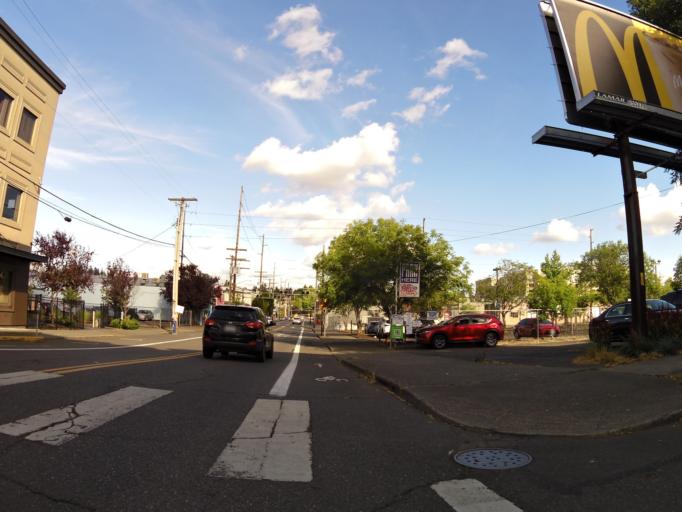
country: US
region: Washington
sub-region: Thurston County
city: Olympia
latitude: 47.0434
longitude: -122.8978
